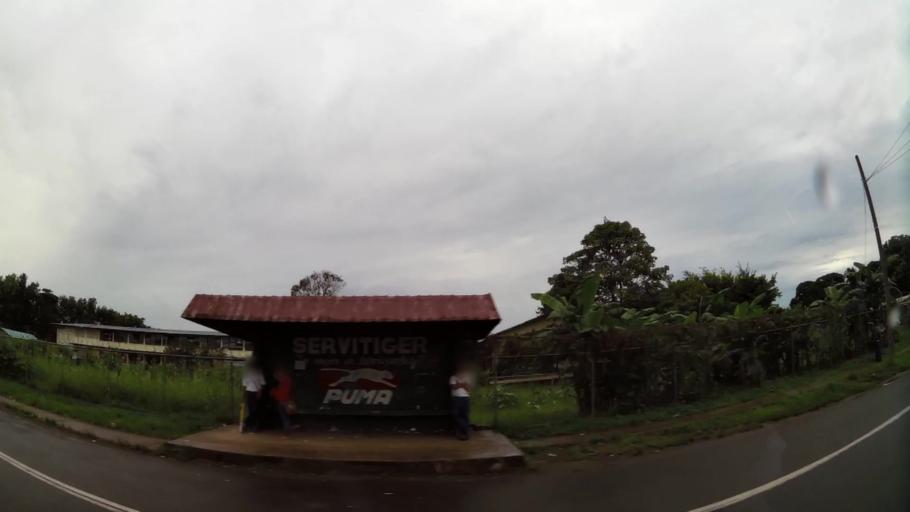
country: PA
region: Veraguas
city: Santiago de Veraguas
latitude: 8.1070
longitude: -80.9772
